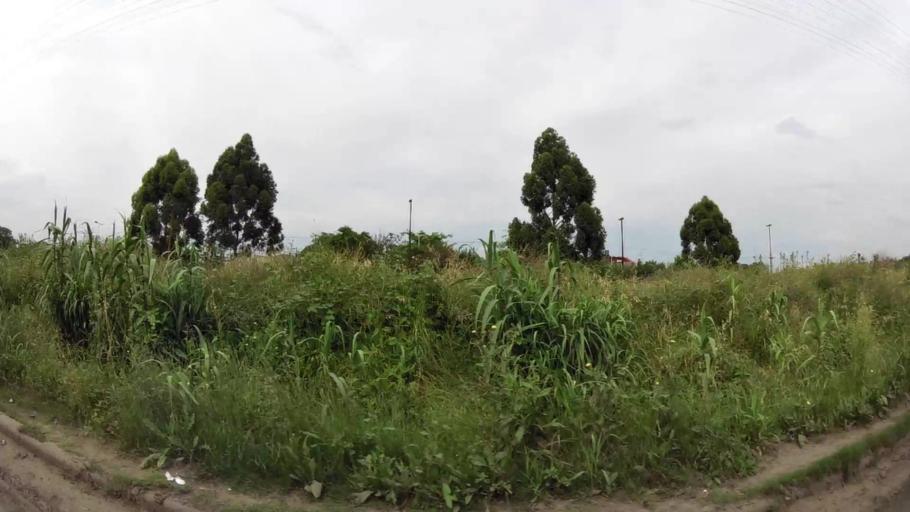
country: AR
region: Buenos Aires
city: San Justo
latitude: -34.6958
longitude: -58.5242
